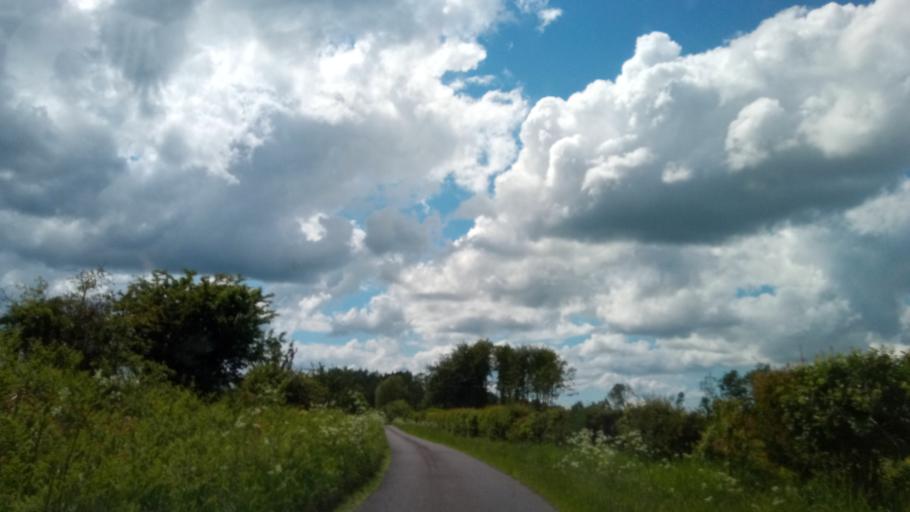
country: GB
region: Scotland
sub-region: The Scottish Borders
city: Coldstream
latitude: 55.5944
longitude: -2.2843
